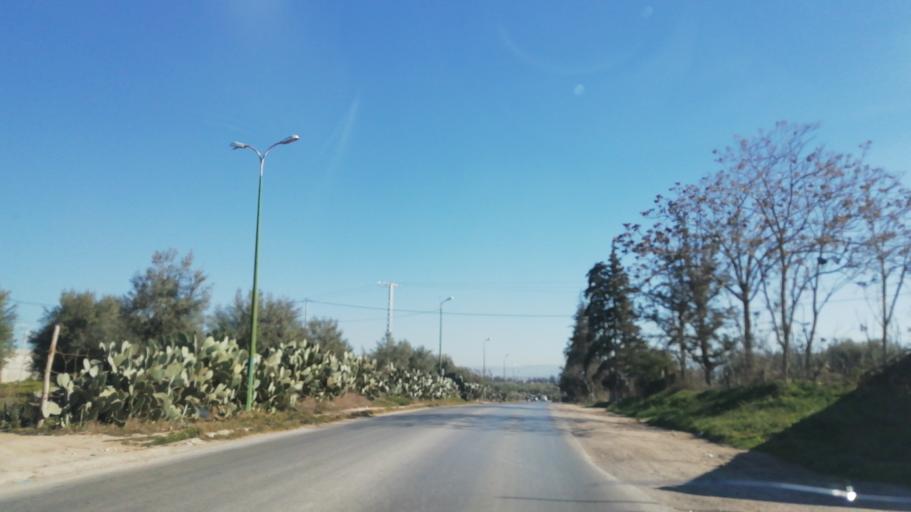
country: DZ
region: Tlemcen
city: Nedroma
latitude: 34.8418
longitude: -1.7150
